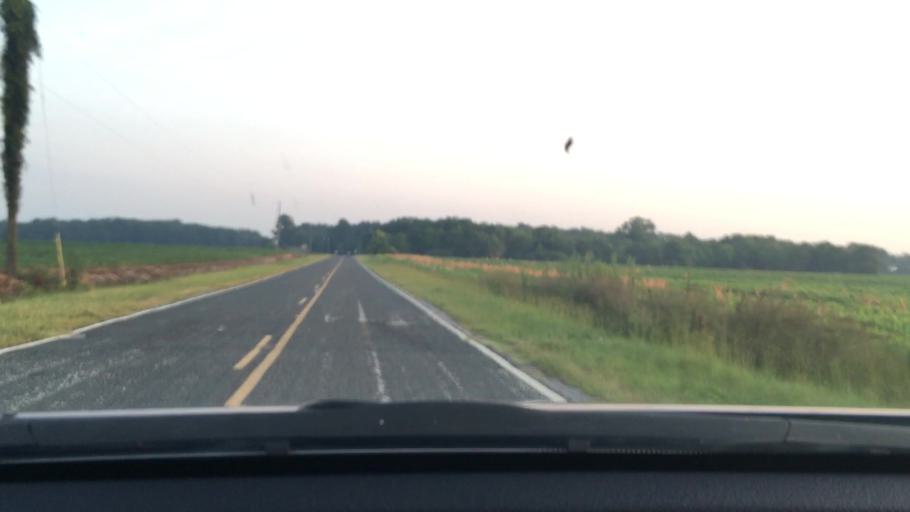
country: US
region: South Carolina
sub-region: Lee County
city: Bishopville
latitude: 34.2638
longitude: -80.1359
